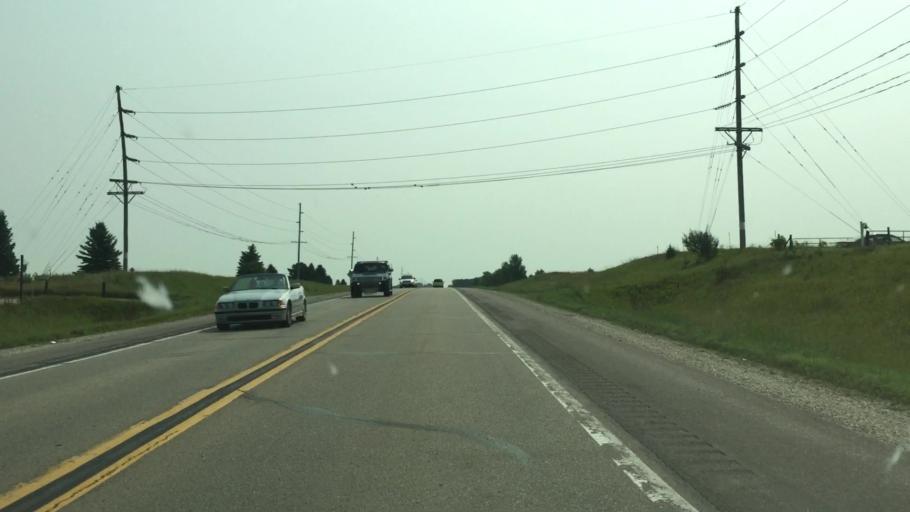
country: US
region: Iowa
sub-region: Dickinson County
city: Milford
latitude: 43.3424
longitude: -95.1727
